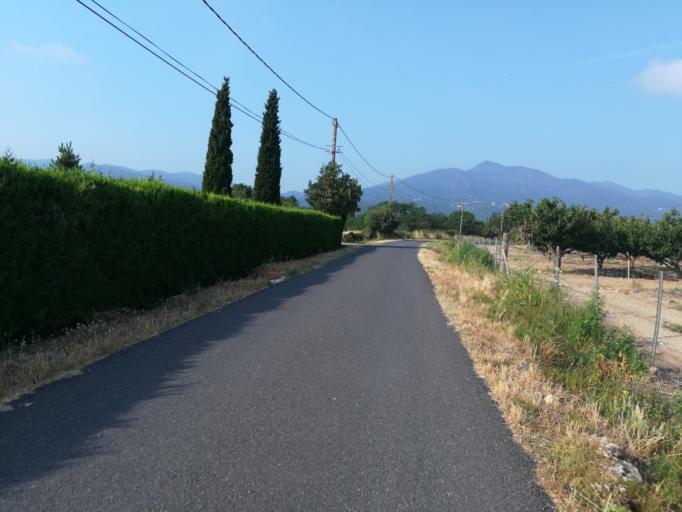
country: FR
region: Languedoc-Roussillon
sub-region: Departement des Pyrenees-Orientales
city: Maureillas-las-Illas
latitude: 42.4991
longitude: 2.8083
